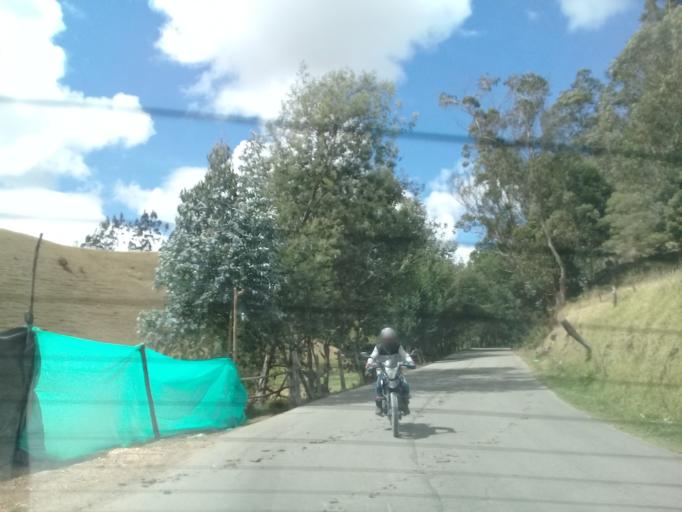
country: CO
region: Cundinamarca
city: Choconta
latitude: 5.1483
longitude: -73.6973
